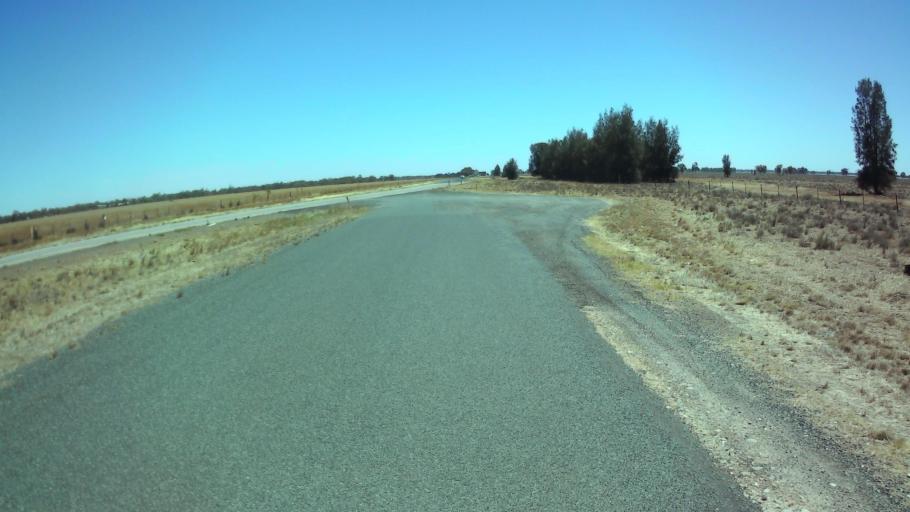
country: AU
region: New South Wales
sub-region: Bland
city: West Wyalong
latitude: -33.7528
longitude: 147.5268
